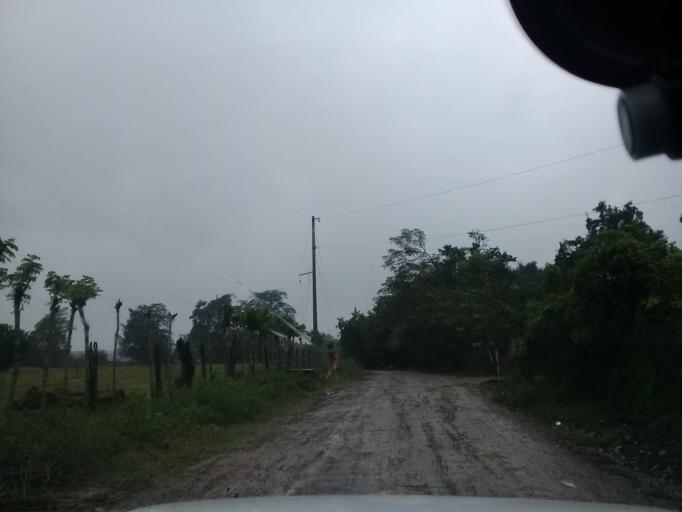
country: MX
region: Veracruz
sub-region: Chalma
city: San Pedro Coyutla
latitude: 21.2486
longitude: -98.4644
